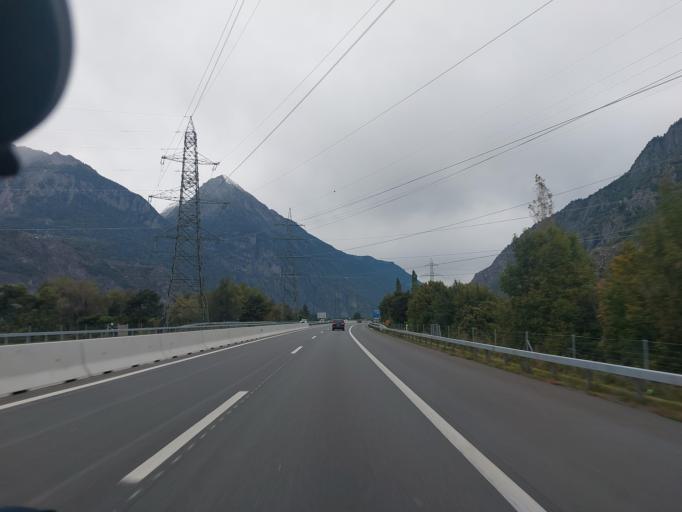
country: CH
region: Valais
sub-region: Martigny District
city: Martigny-Ville
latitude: 46.1188
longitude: 7.0698
